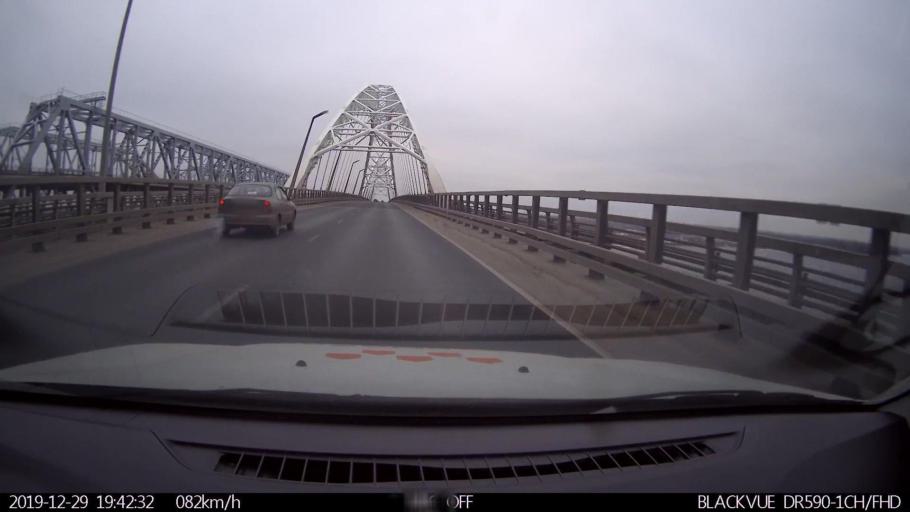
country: RU
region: Nizjnij Novgorod
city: Nizhniy Novgorod
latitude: 56.3513
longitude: 43.9235
